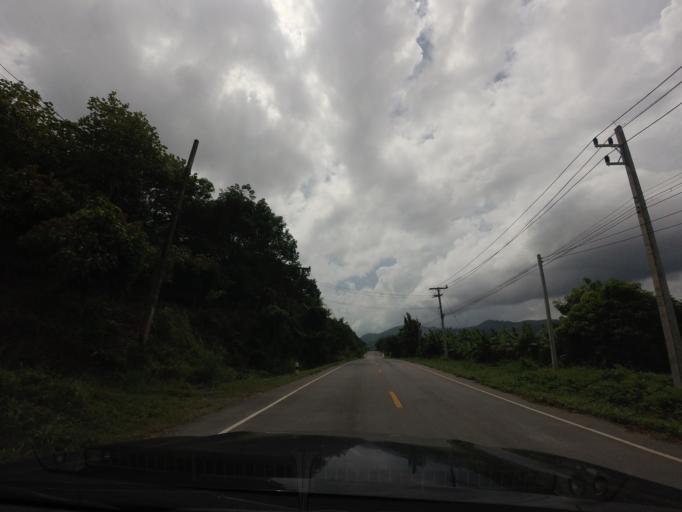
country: TH
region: Loei
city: Pak Chom
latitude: 18.0633
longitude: 101.7830
